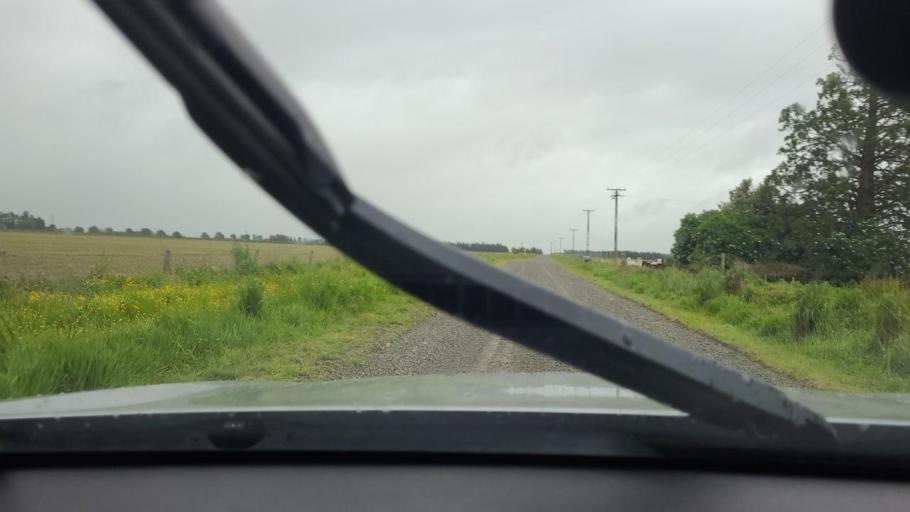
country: NZ
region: Southland
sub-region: Southland District
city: Winton
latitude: -46.1041
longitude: 168.2471
